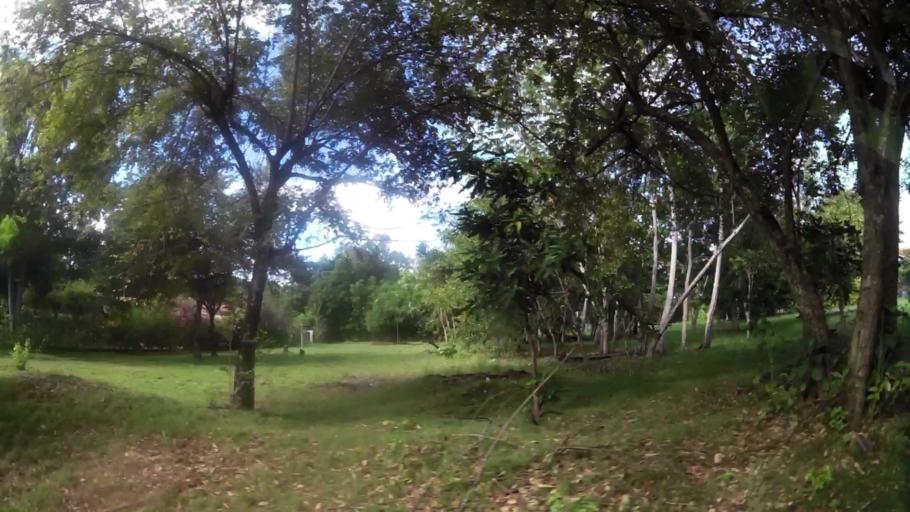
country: PA
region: Panama
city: Nueva Gorgona
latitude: 8.5309
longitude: -79.8881
